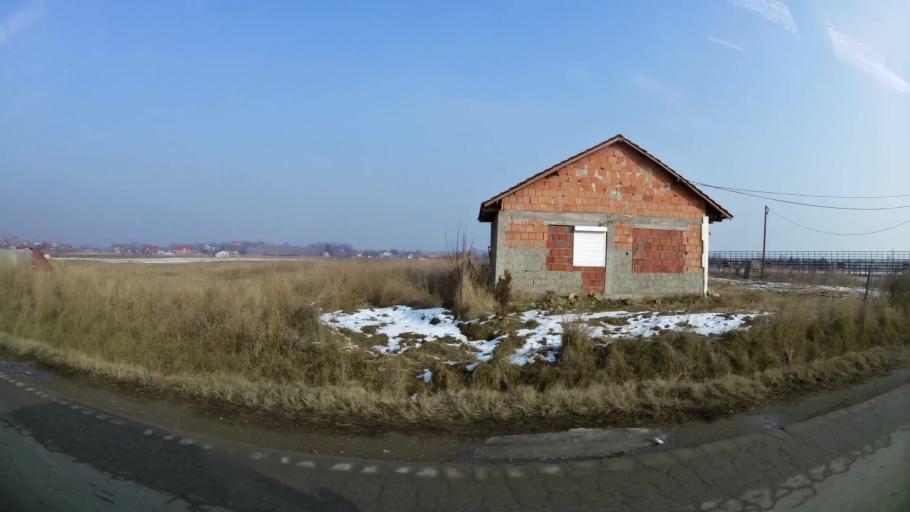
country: MK
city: Kadino
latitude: 41.9770
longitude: 21.5939
